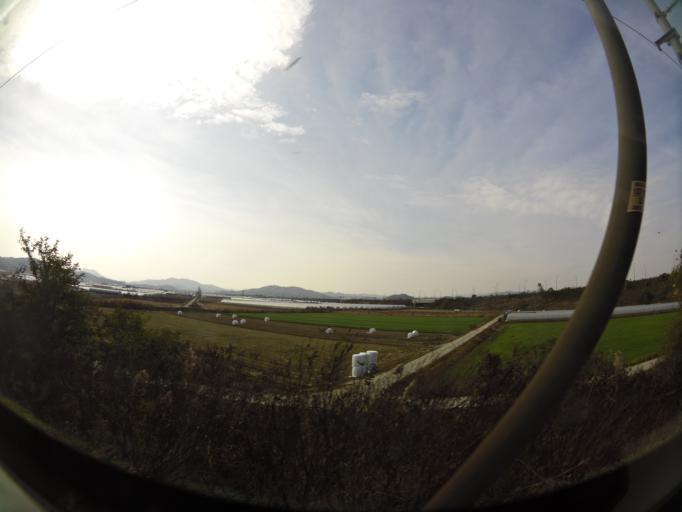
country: KR
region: Daejeon
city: Songgang-dong
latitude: 36.5688
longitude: 127.3166
